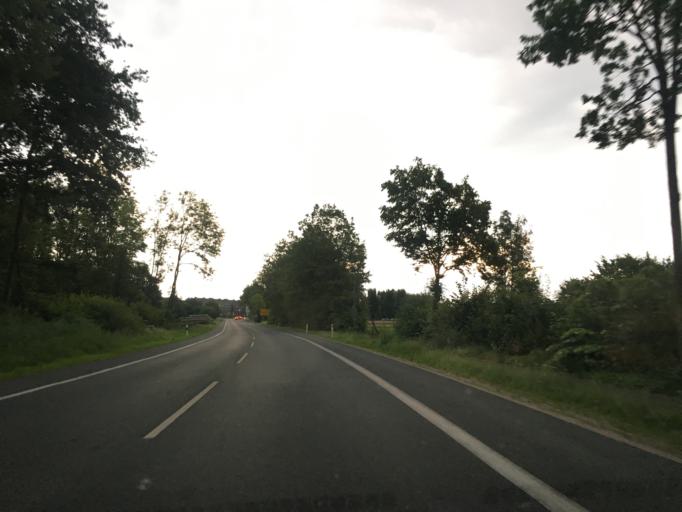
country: DE
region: North Rhine-Westphalia
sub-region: Regierungsbezirk Munster
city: Muenster
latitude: 51.9078
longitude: 7.6848
